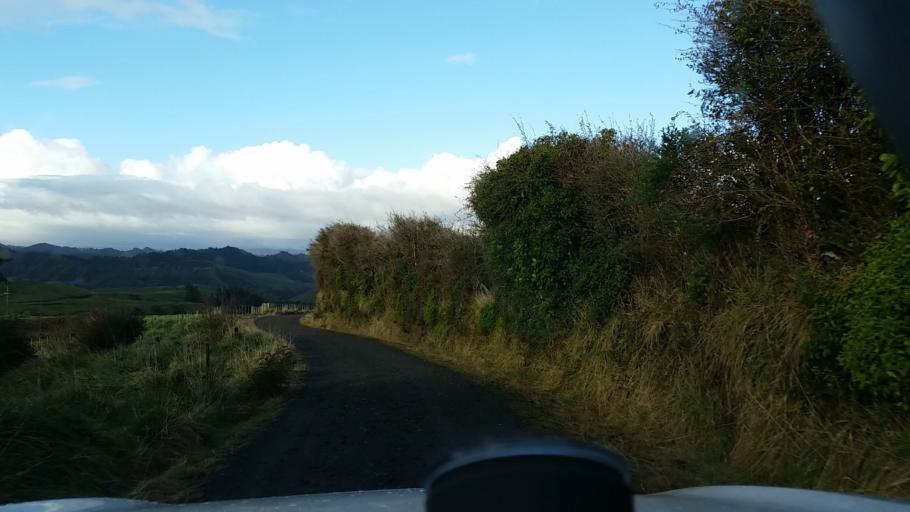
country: NZ
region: Taranaki
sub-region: South Taranaki District
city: Eltham
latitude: -39.4087
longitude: 174.5702
